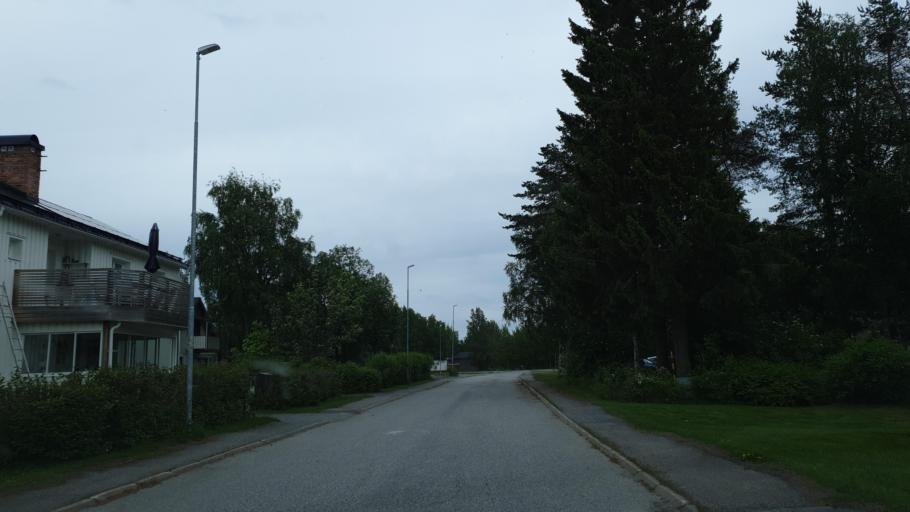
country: SE
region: Vaesterbotten
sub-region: Sorsele Kommun
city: Sorsele
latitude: 65.5360
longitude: 17.5286
